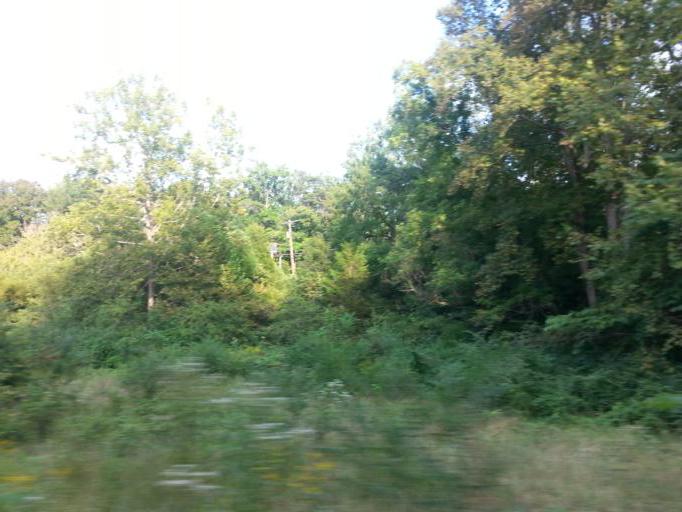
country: US
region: Tennessee
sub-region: Knox County
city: Knoxville
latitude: 35.8934
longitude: -83.8724
